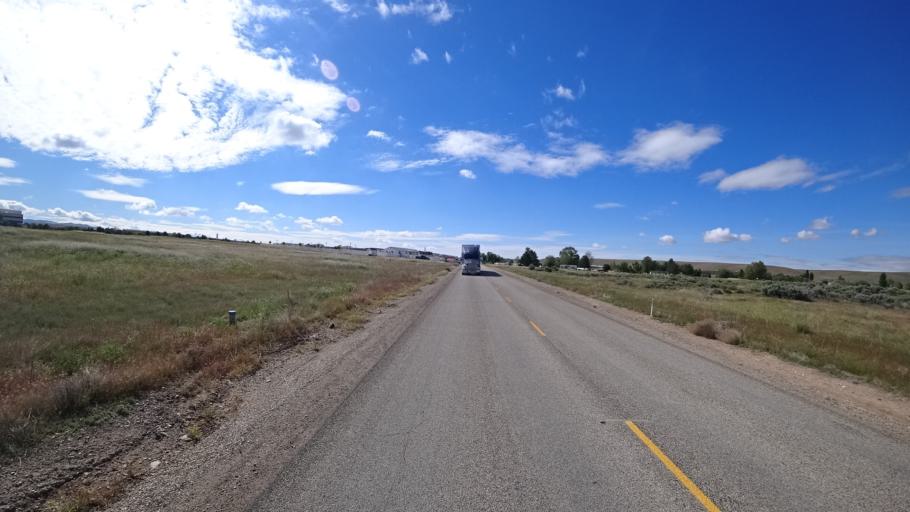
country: US
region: Idaho
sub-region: Ada County
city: Boise
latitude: 43.5300
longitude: -116.1571
